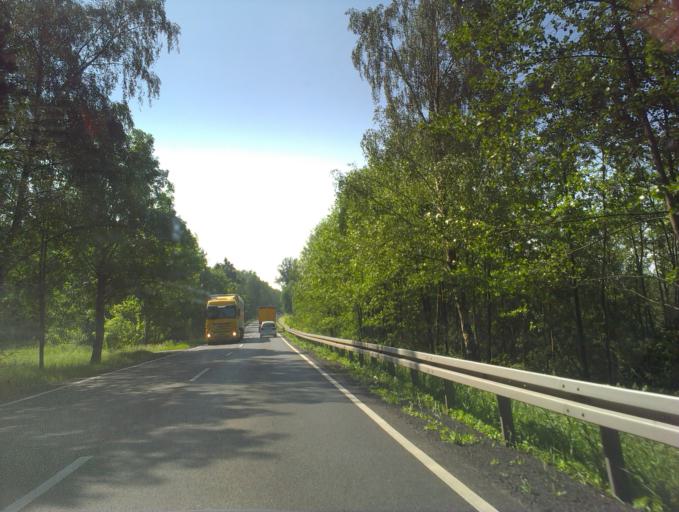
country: PL
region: Greater Poland Voivodeship
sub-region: Powiat zlotowski
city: Okonek
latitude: 53.5227
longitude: 16.8529
